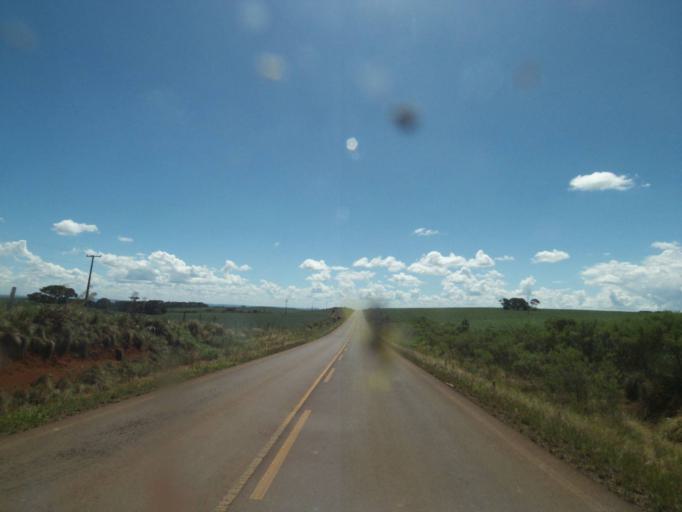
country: BR
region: Parana
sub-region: Pinhao
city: Pinhao
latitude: -25.8132
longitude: -52.0553
